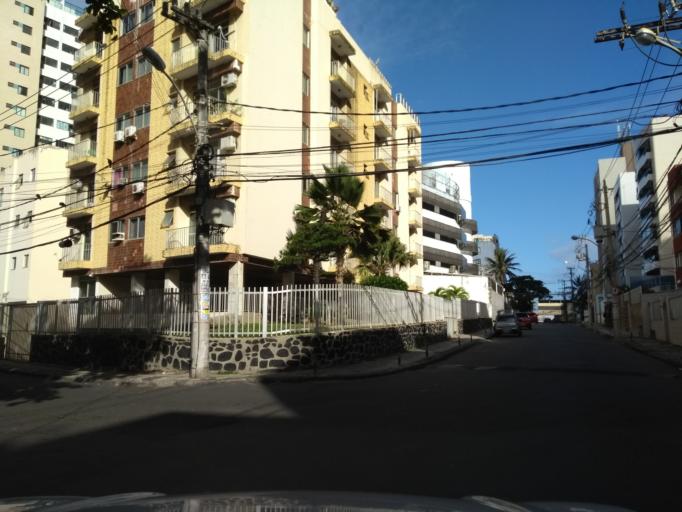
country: BR
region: Bahia
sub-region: Salvador
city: Salvador
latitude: -12.9990
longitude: -38.4516
